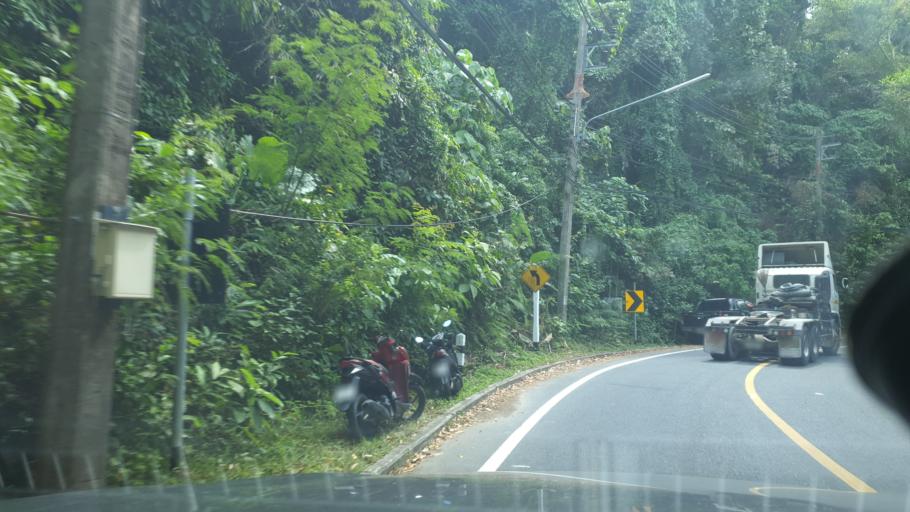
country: TH
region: Phuket
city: Thalang
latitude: 8.0414
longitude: 98.2769
